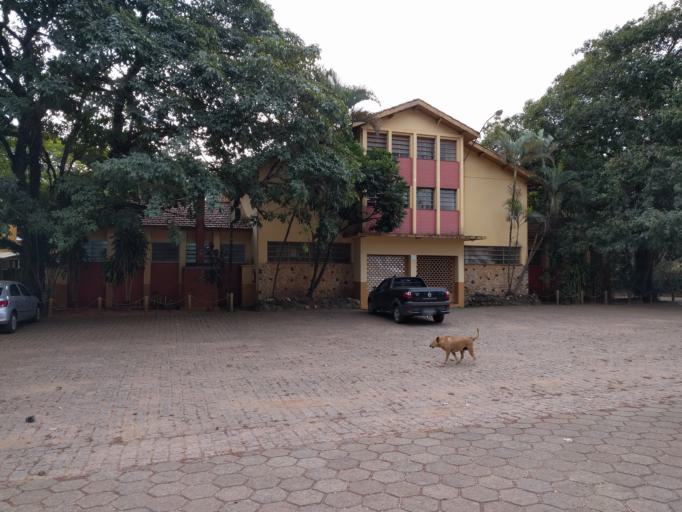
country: BR
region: Sao Paulo
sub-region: Paranapanema
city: Paranapanema
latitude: -23.4322
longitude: -48.8736
